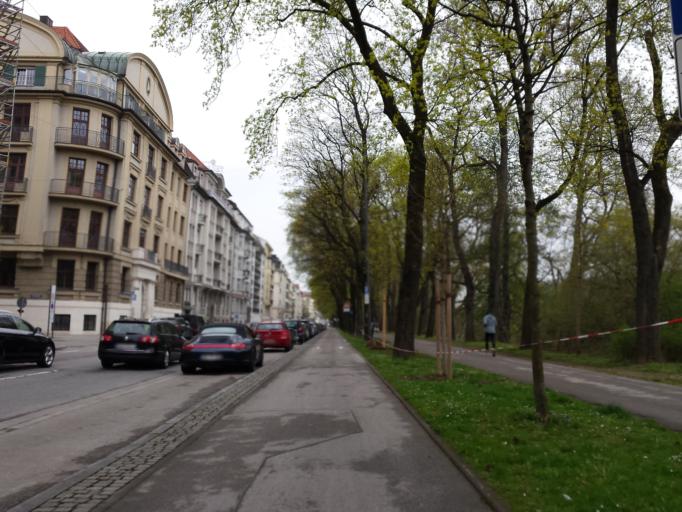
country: DE
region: Bavaria
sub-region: Upper Bavaria
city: Munich
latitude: 48.1435
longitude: 11.5951
